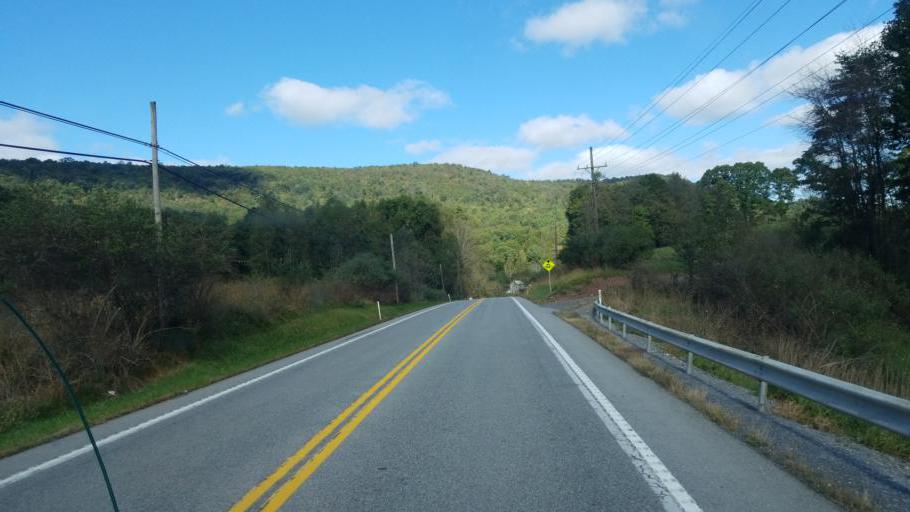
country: US
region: Pennsylvania
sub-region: Fulton County
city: McConnellsburg
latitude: 39.9518
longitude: -78.0234
